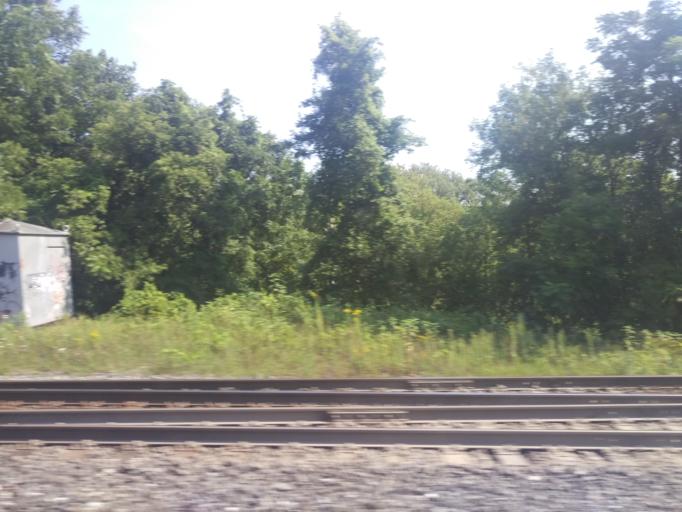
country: CA
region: Ontario
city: Brockville
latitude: 44.5901
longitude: -75.6962
